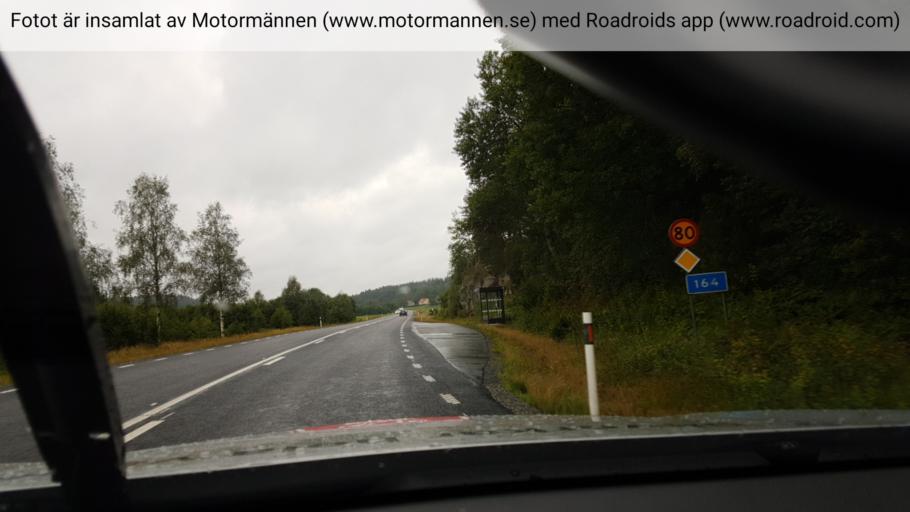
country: SE
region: Vaestra Goetaland
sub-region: Dals-Ed Kommun
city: Ed
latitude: 58.9155
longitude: 12.0207
